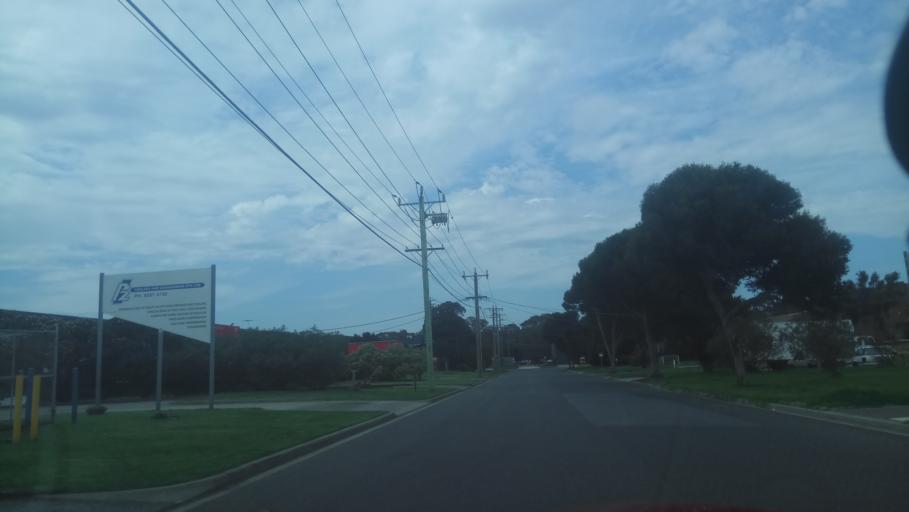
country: AU
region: Victoria
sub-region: Kingston
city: Aspendale Gardens
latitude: -38.0054
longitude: 145.1111
